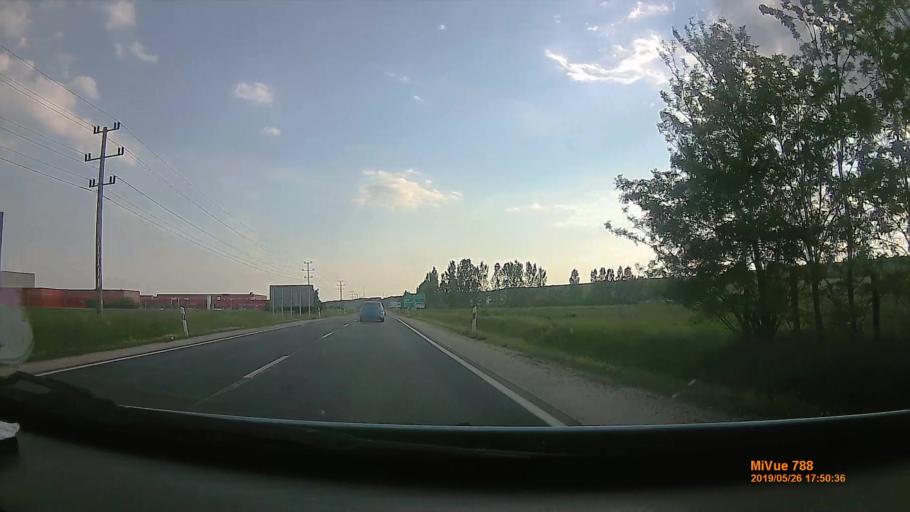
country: HU
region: Borsod-Abauj-Zemplen
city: Szikszo
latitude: 48.1802
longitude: 20.9183
